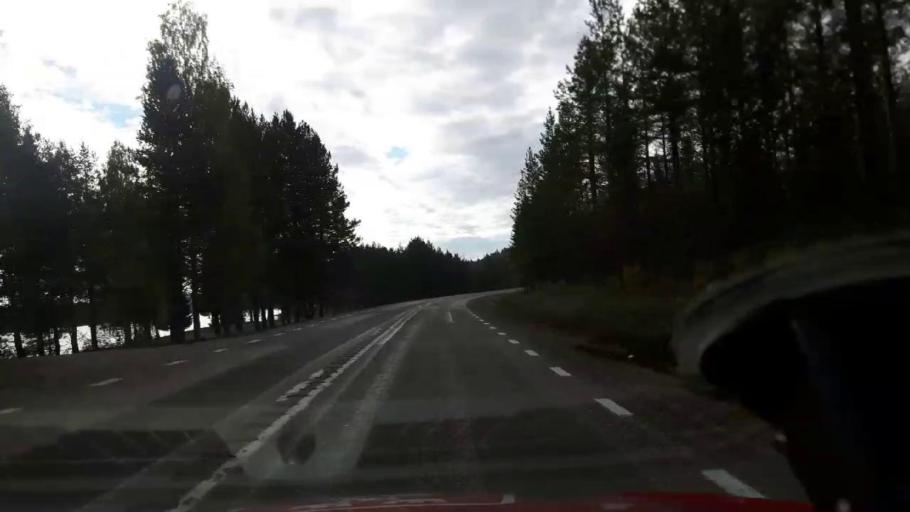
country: SE
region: Gaevleborg
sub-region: Ljusdals Kommun
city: Farila
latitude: 61.9632
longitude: 15.3564
